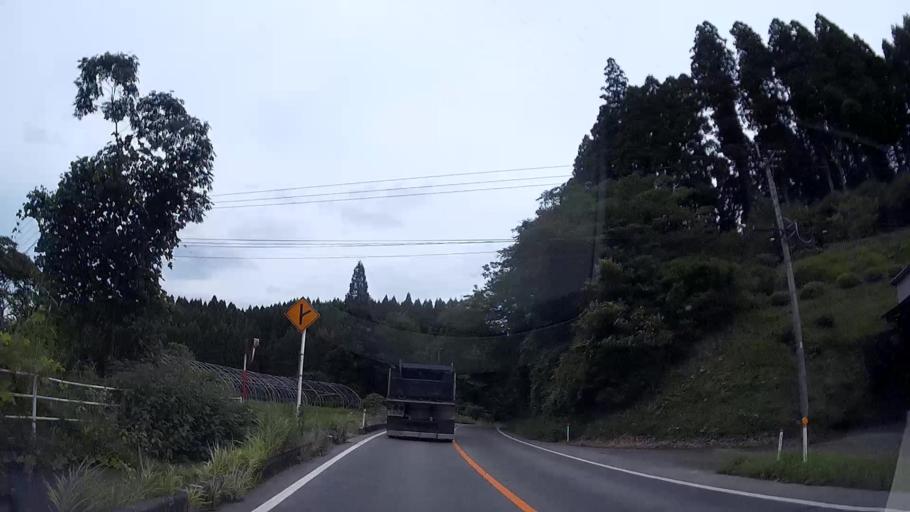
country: JP
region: Oita
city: Tsukawaki
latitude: 33.1239
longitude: 131.0428
